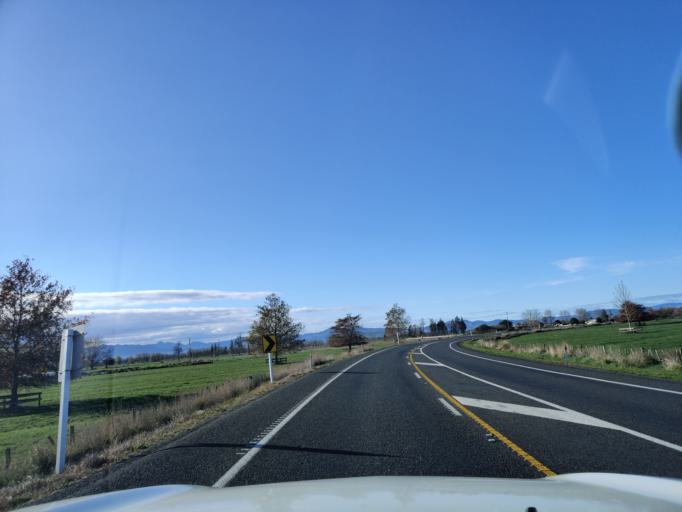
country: NZ
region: Waikato
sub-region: Hauraki District
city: Ngatea
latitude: -37.2718
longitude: 175.5286
